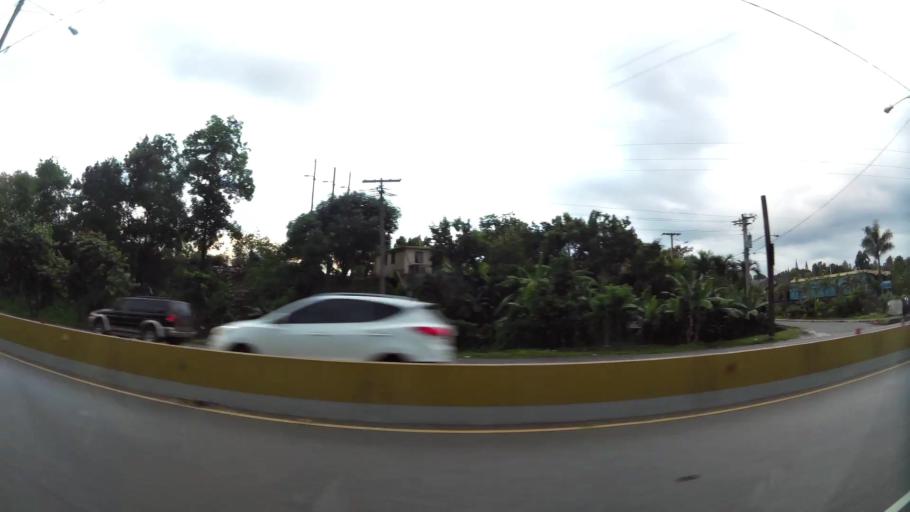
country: DO
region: Santo Domingo
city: Santo Domingo Oeste
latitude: 18.5659
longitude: -70.0823
